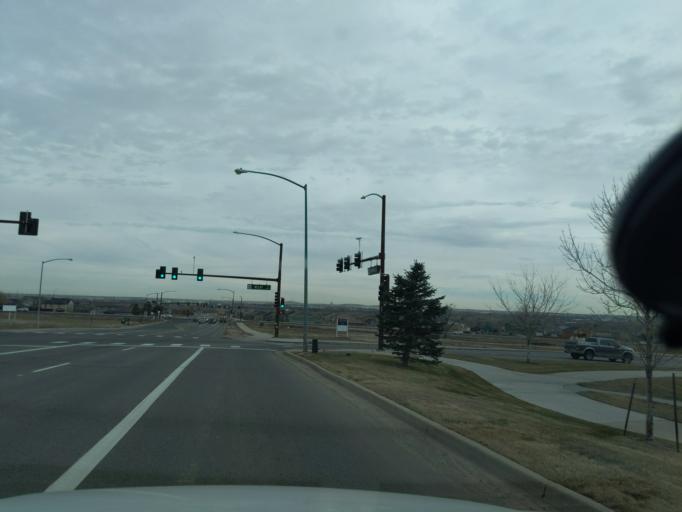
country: US
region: Colorado
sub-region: Adams County
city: Thornton
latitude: 39.8703
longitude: -104.9432
